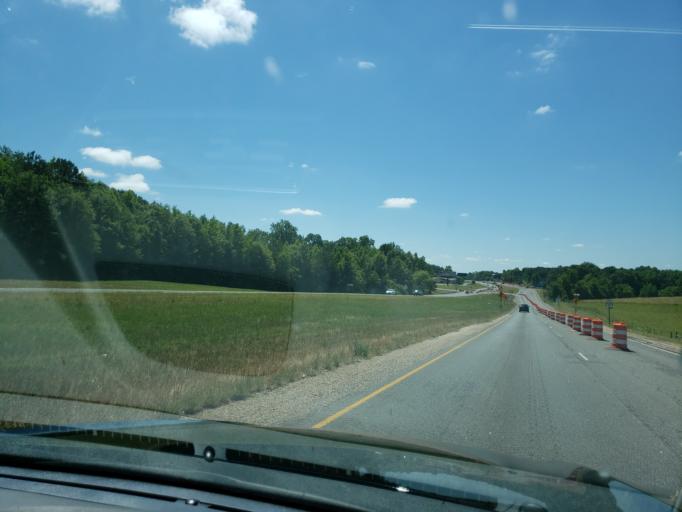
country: US
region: Alabama
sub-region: Lee County
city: Auburn
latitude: 32.6836
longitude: -85.4936
